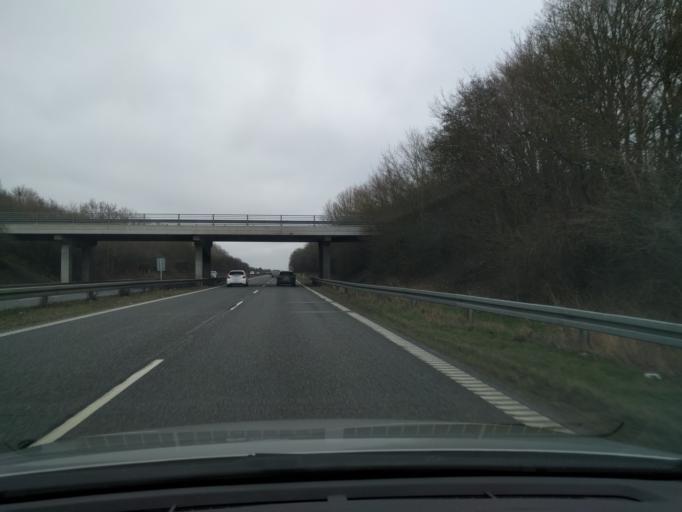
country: DK
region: Zealand
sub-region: Slagelse Kommune
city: Korsor
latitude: 55.3596
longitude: 11.1728
